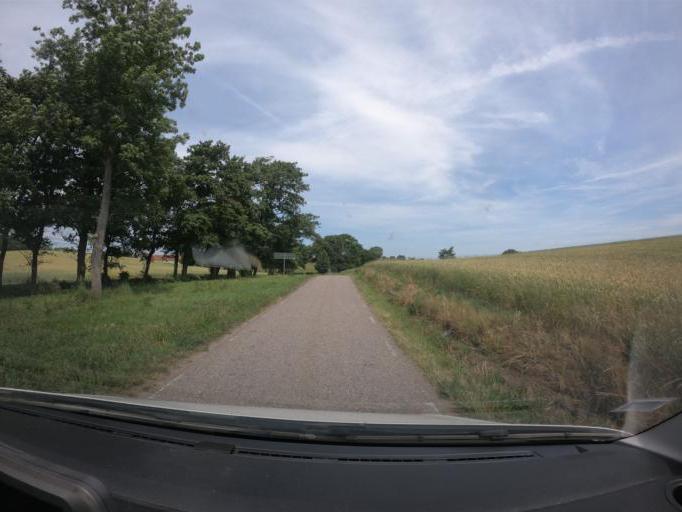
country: SE
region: Skane
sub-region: Angelholms Kommun
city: Vejbystrand
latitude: 56.3667
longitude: 12.7358
